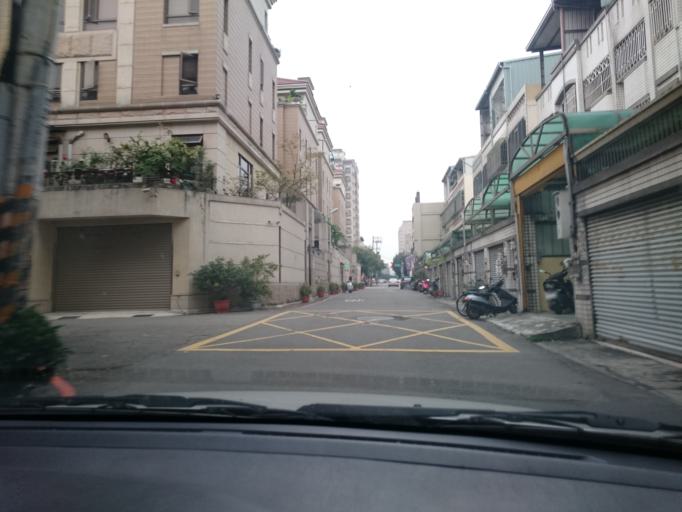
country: TW
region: Taiwan
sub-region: Taichung City
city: Taichung
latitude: 24.1735
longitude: 120.6386
